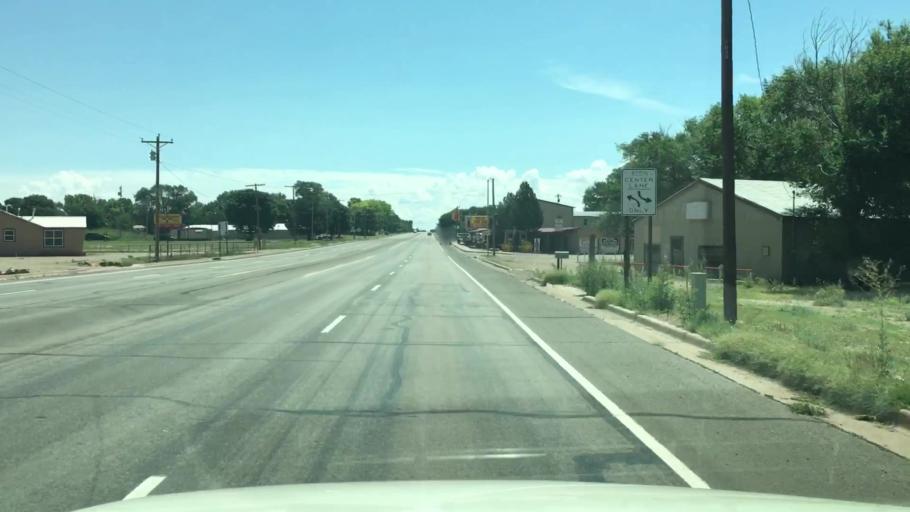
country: US
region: New Mexico
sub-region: De Baca County
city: Fort Sumner
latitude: 34.4669
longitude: -104.2307
